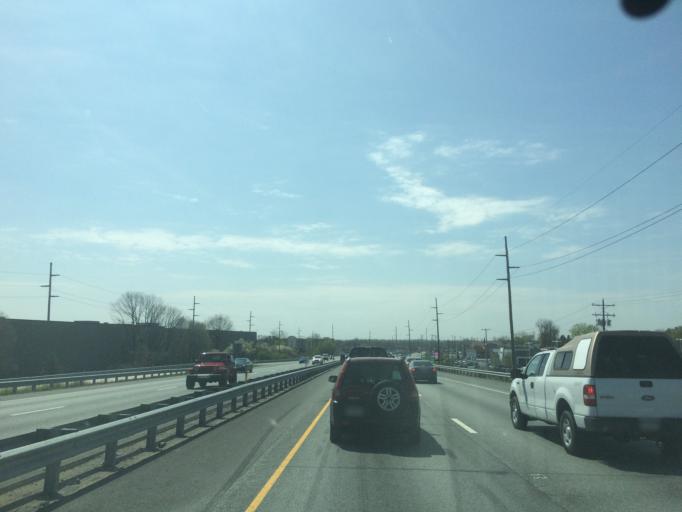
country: US
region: Pennsylvania
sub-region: York County
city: East York
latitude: 39.9835
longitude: -76.6862
